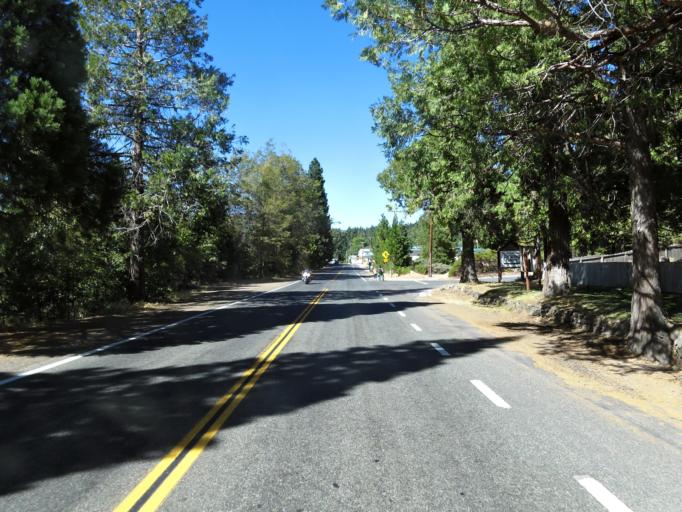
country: US
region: California
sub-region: Siskiyou County
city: Mount Shasta
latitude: 41.2992
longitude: -122.3062
